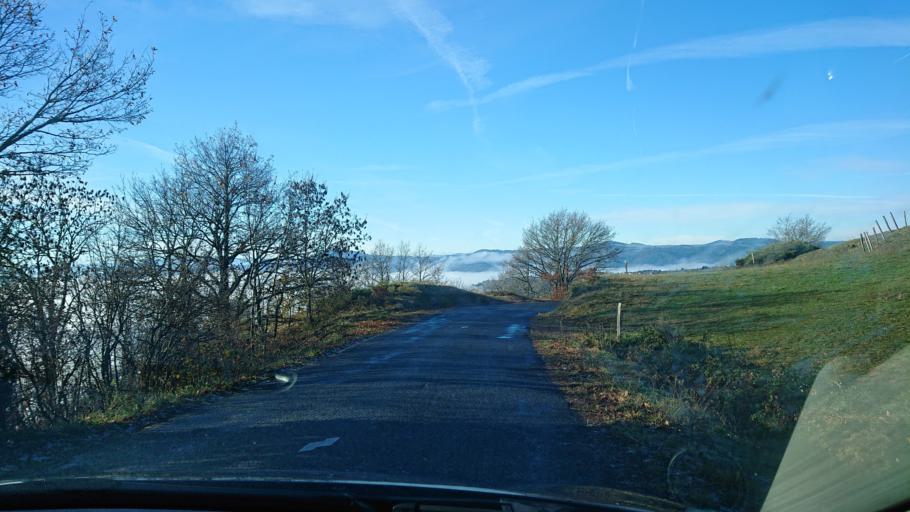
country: FR
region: Auvergne
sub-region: Departement de la Haute-Loire
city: Vorey
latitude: 45.2139
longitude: 3.9351
